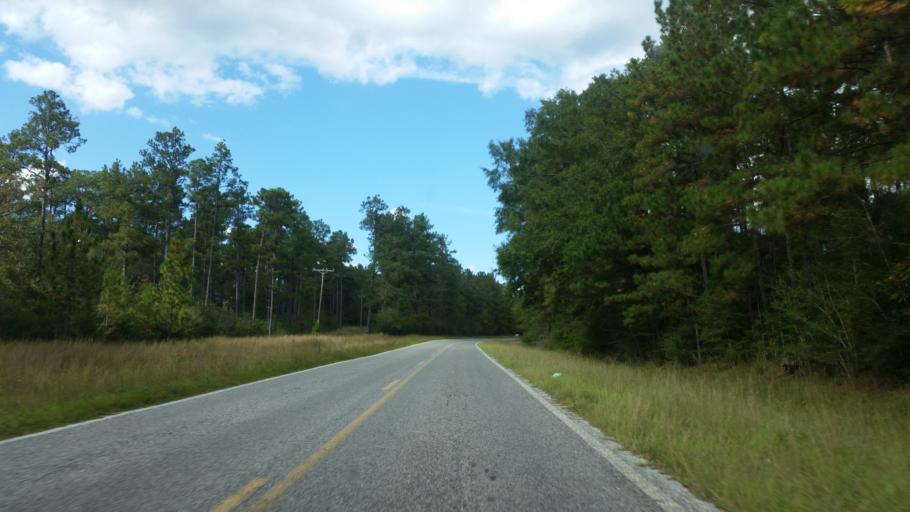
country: US
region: Mississippi
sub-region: Stone County
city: Wiggins
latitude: 30.9766
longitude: -89.0568
